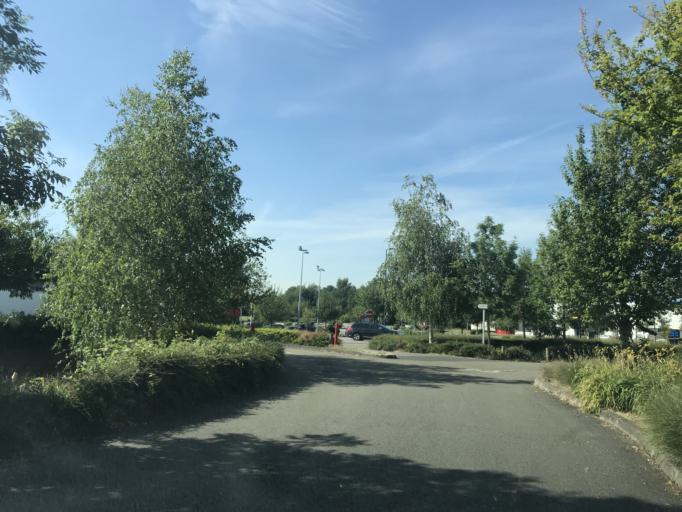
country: FR
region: Haute-Normandie
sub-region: Departement de la Seine-Maritime
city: Roumare
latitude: 49.5276
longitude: 0.9668
